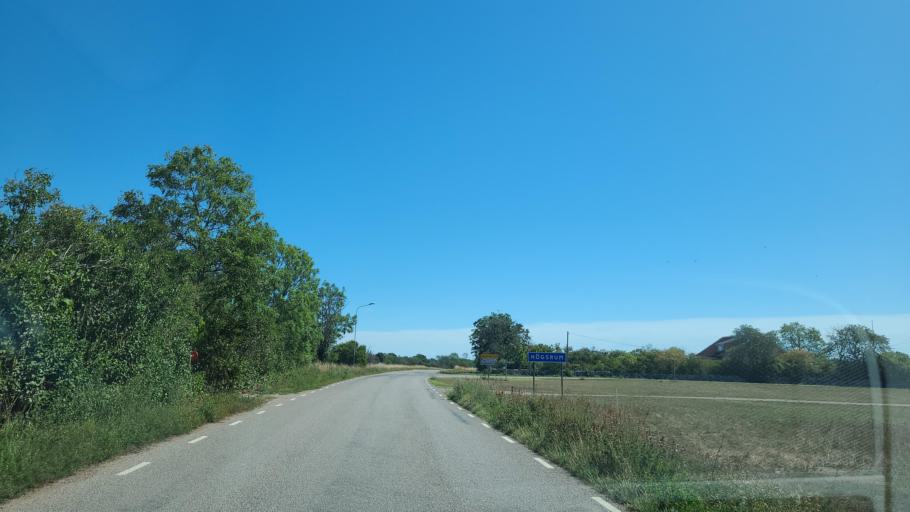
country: SE
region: Kalmar
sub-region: Borgholms Kommun
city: Borgholm
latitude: 56.7671
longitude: 16.5951
